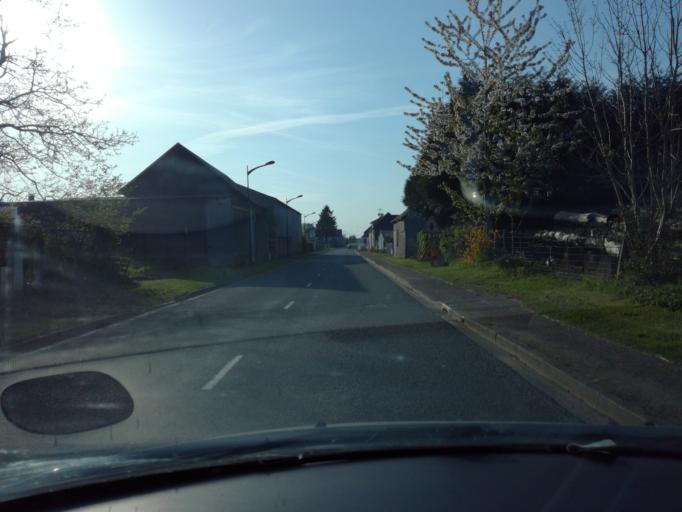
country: FR
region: Picardie
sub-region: Departement de la Somme
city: Hornoy-le-Bourg
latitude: 49.8268
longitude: 1.9396
